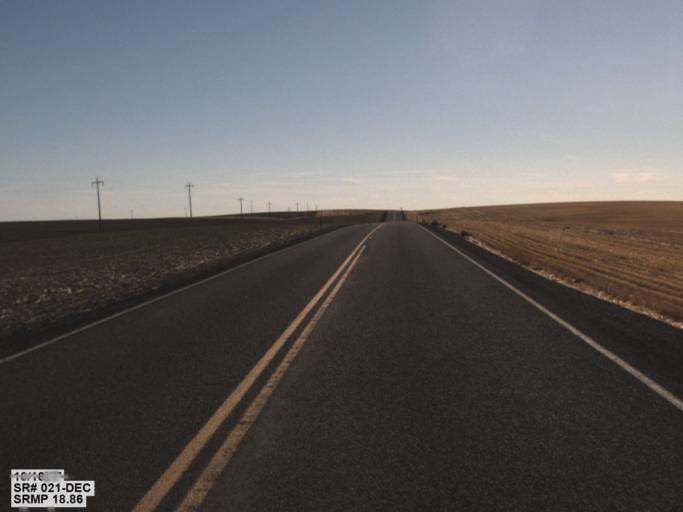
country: US
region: Washington
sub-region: Adams County
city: Ritzville
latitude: 46.8934
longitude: -118.5689
